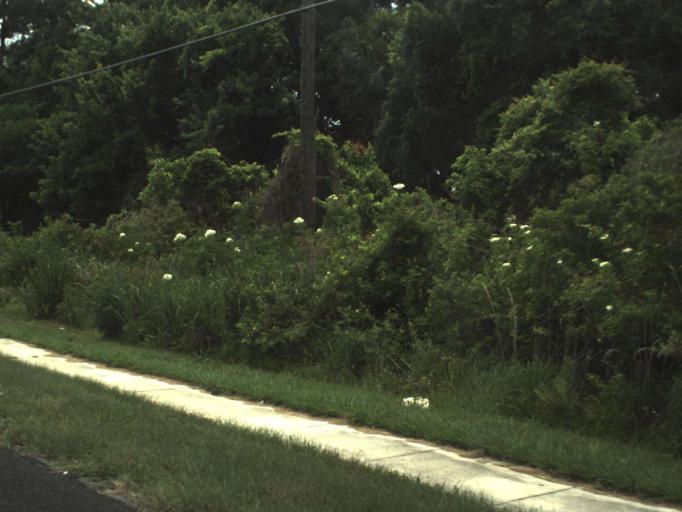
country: US
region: Florida
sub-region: Seminole County
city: Lake Mary
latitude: 28.7541
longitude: -81.2887
